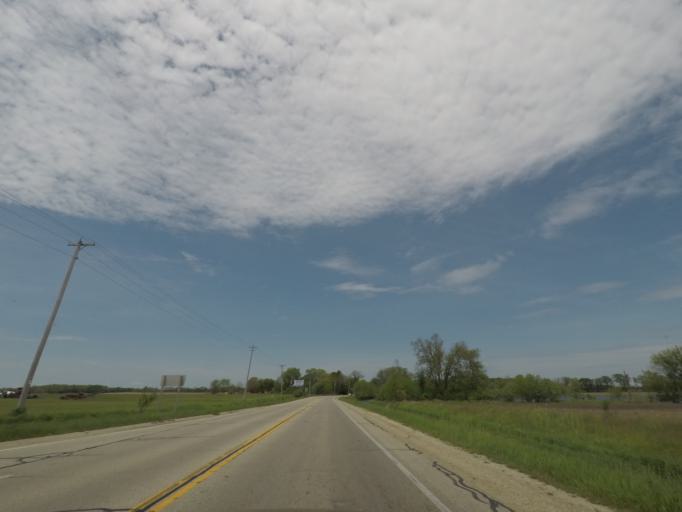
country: US
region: Wisconsin
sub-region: Green County
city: Brooklyn
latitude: 42.8549
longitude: -89.3417
